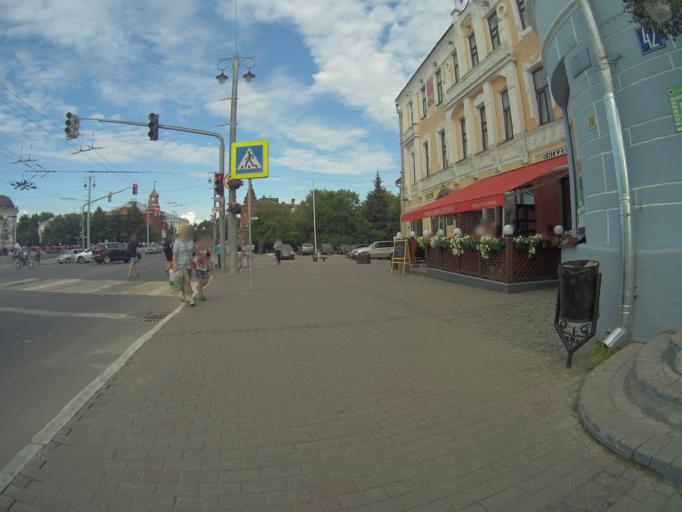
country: RU
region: Vladimir
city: Vladimir
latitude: 56.1283
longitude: 40.4043
